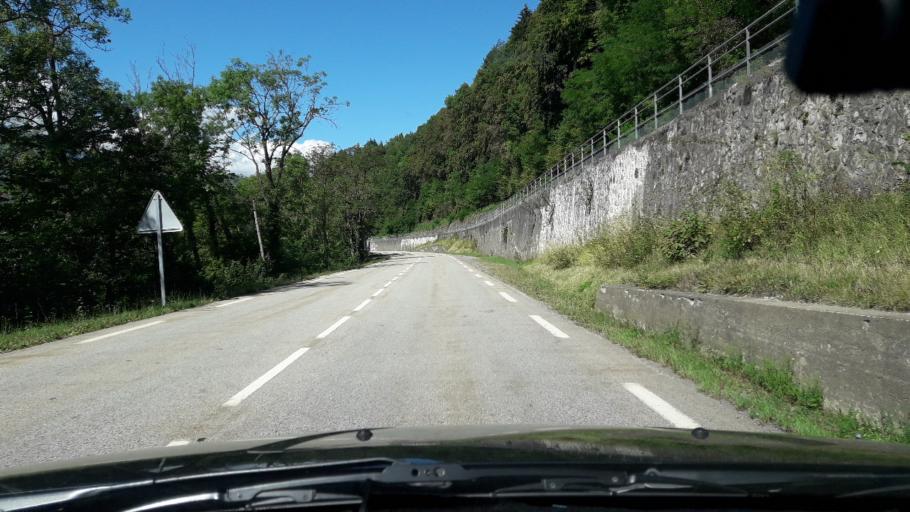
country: FR
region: Rhone-Alpes
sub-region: Departement de l'Isere
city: La Motte-Saint-Martin
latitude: 44.9397
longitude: 5.6406
